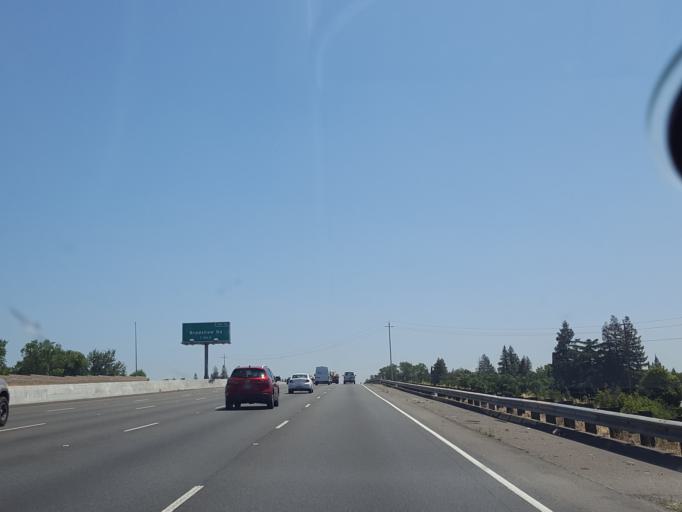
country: US
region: California
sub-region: Sacramento County
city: La Riviera
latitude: 38.5604
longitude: -121.3626
